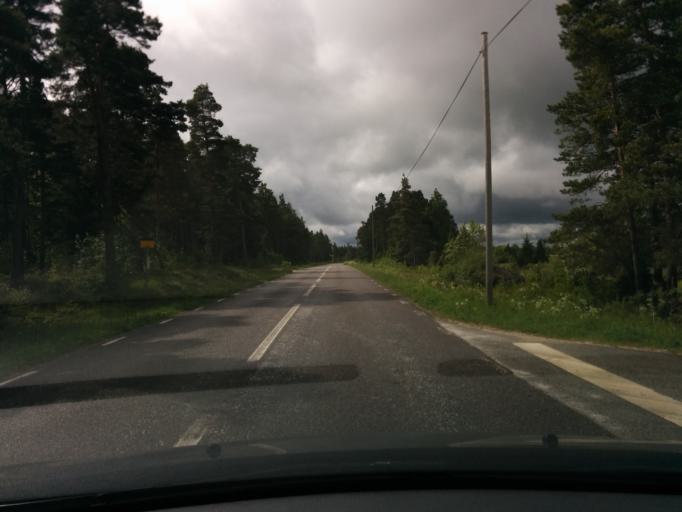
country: SE
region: Gotland
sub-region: Gotland
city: Slite
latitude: 57.5975
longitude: 18.7367
